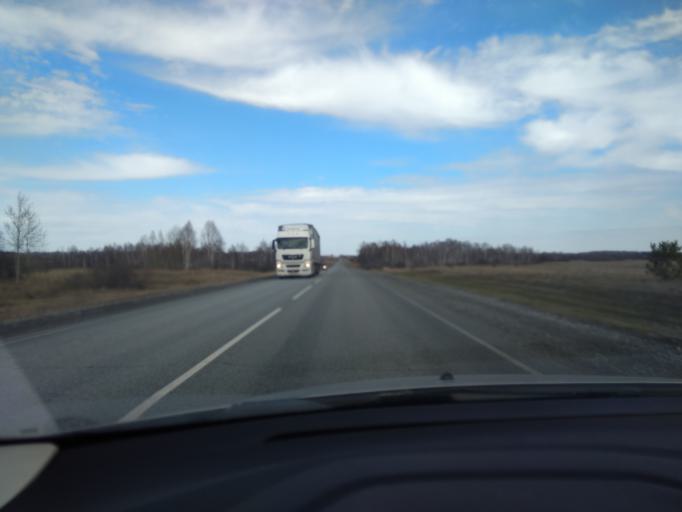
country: RU
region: Sverdlovsk
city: Pyshma
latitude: 56.9876
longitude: 63.2648
